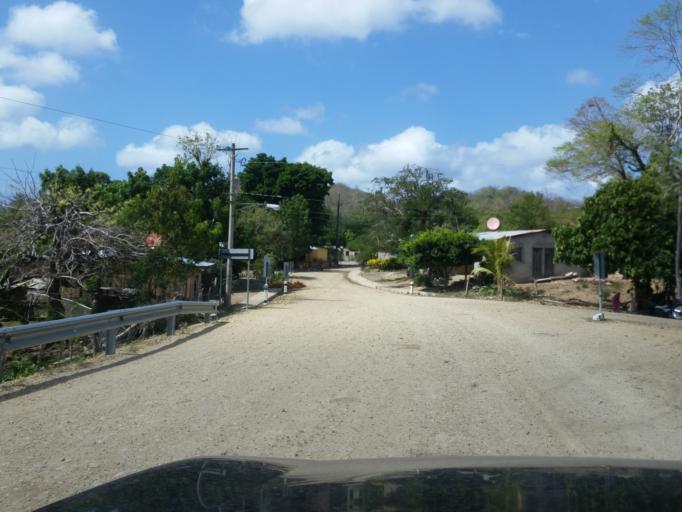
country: CR
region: Guanacaste
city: La Cruz
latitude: 11.1122
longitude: -85.7597
